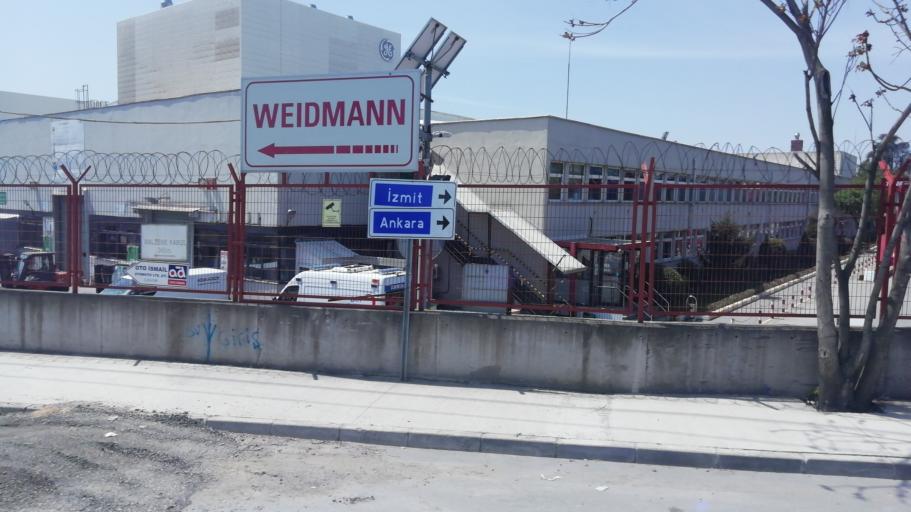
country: TR
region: Kocaeli
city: Gebze
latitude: 40.7981
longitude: 29.4490
